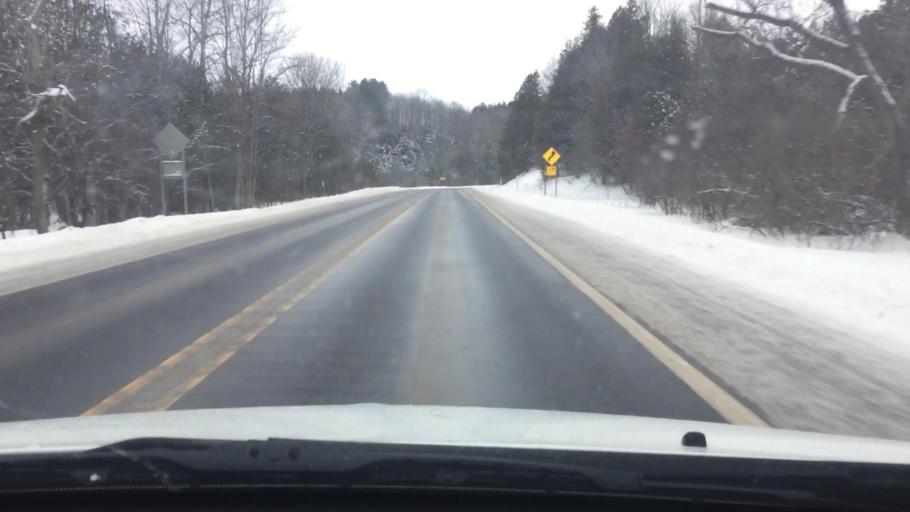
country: US
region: Michigan
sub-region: Charlevoix County
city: East Jordan
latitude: 45.1285
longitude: -85.0765
